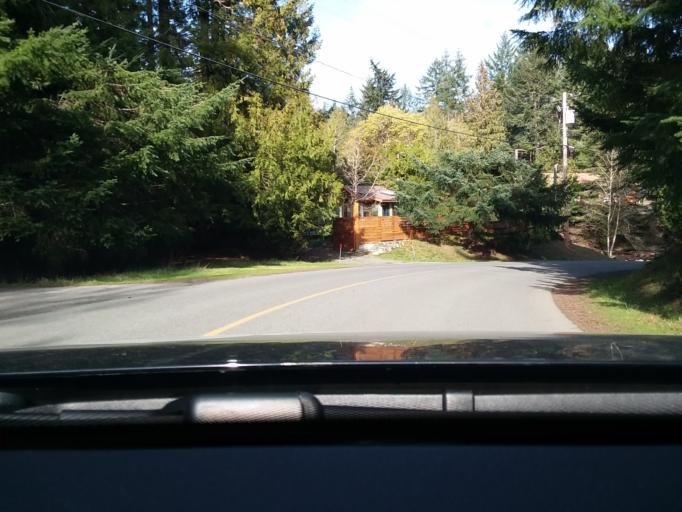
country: CA
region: British Columbia
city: North Saanich
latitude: 48.7722
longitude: -123.2901
